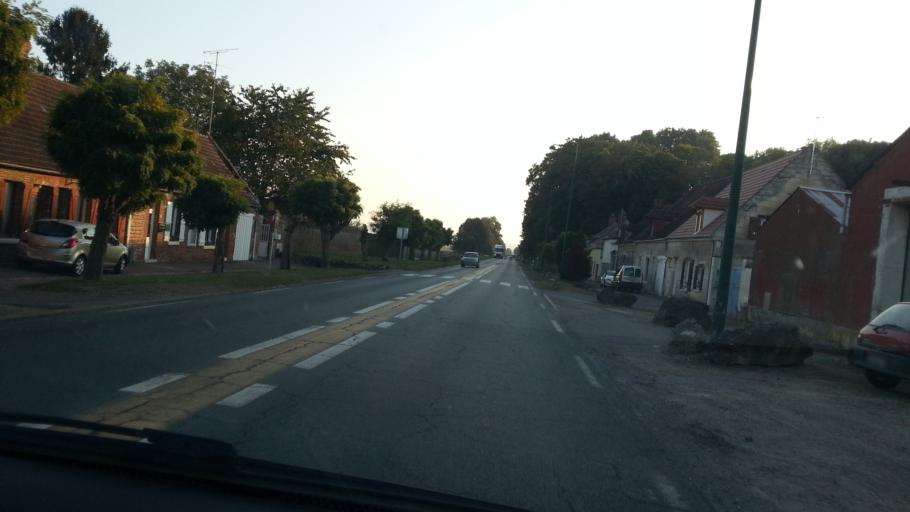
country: FR
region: Picardie
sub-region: Departement de l'Oise
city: Grandfresnoy
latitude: 49.3831
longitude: 2.6198
